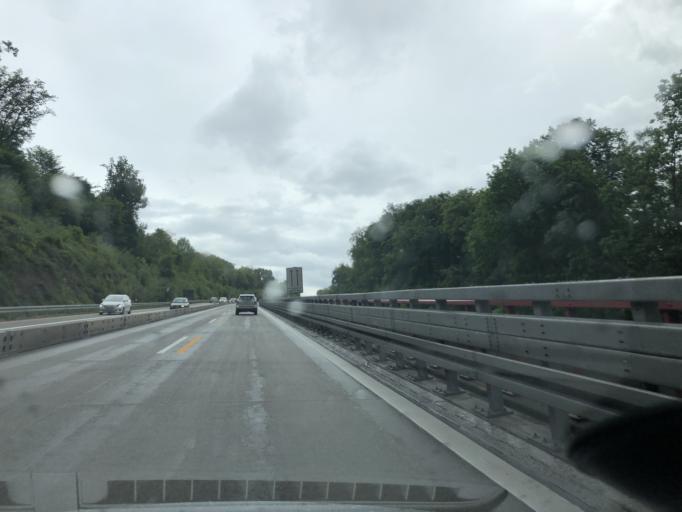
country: DE
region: Baden-Wuerttemberg
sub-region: Karlsruhe Region
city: Ettlingen
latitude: 48.9682
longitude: 8.4638
